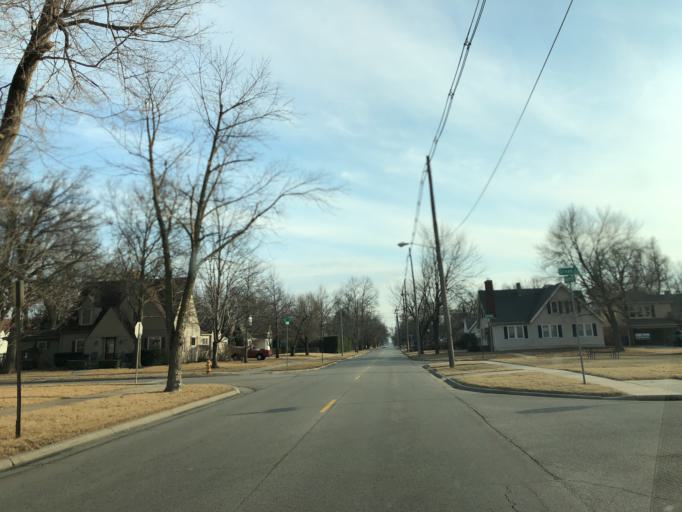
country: US
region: Kansas
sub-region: Reno County
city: Hutchinson
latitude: 38.0781
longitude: -97.9356
